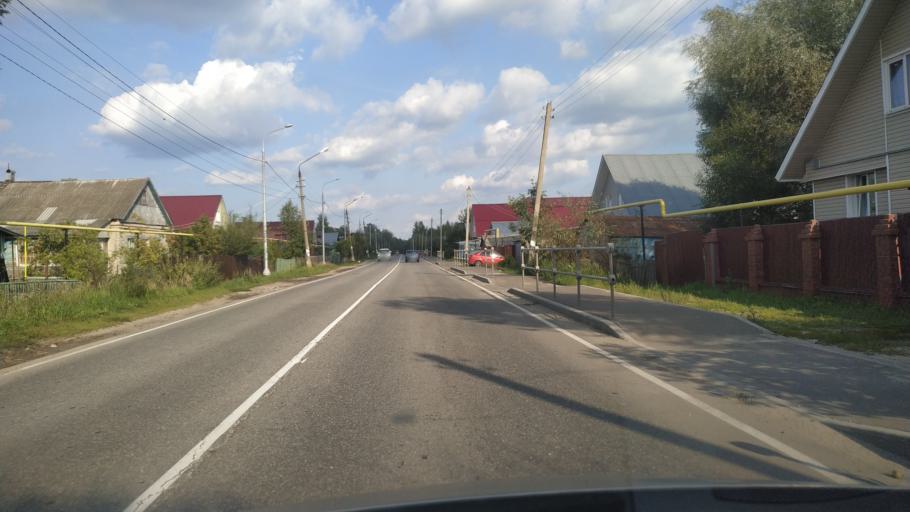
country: RU
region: Moskovskaya
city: Likino-Dulevo
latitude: 55.7298
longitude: 39.0021
